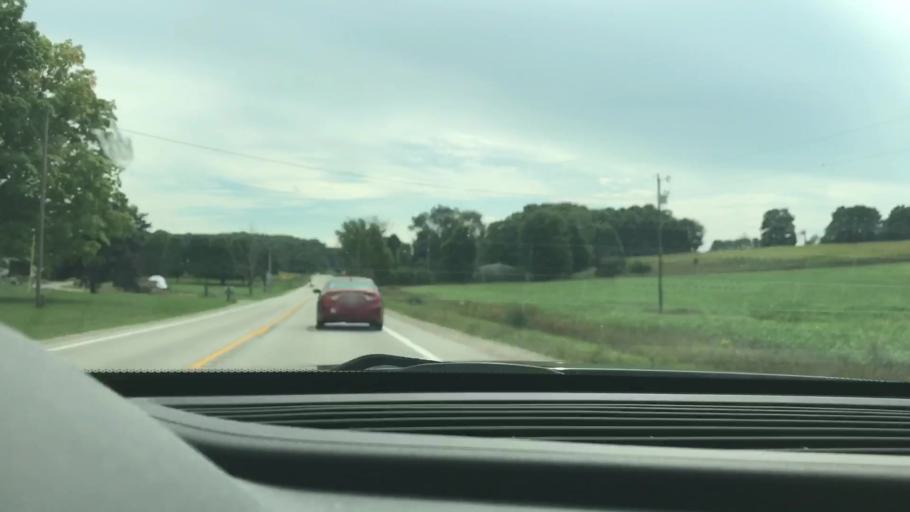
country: US
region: Michigan
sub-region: Antrim County
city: Bellaire
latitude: 45.0912
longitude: -85.2900
